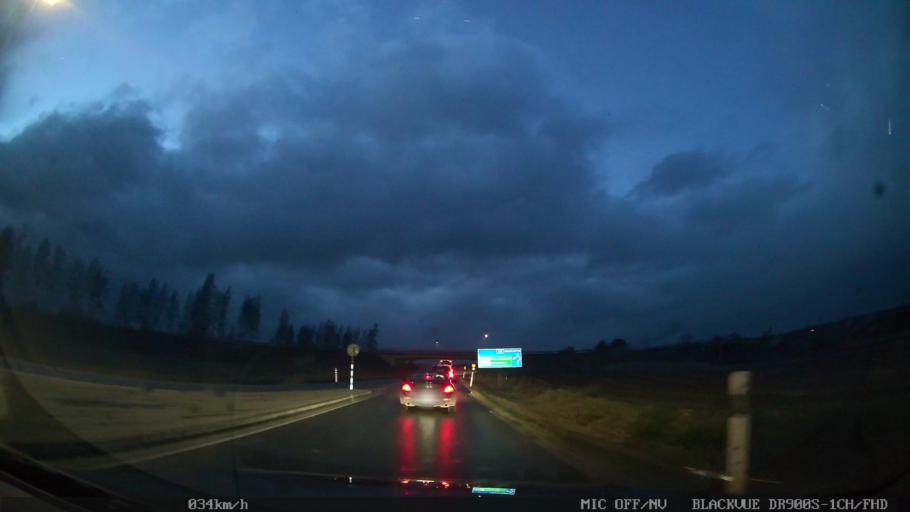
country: SE
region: Skane
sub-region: Hassleholms Kommun
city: Hassleholm
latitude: 56.1798
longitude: 13.7554
